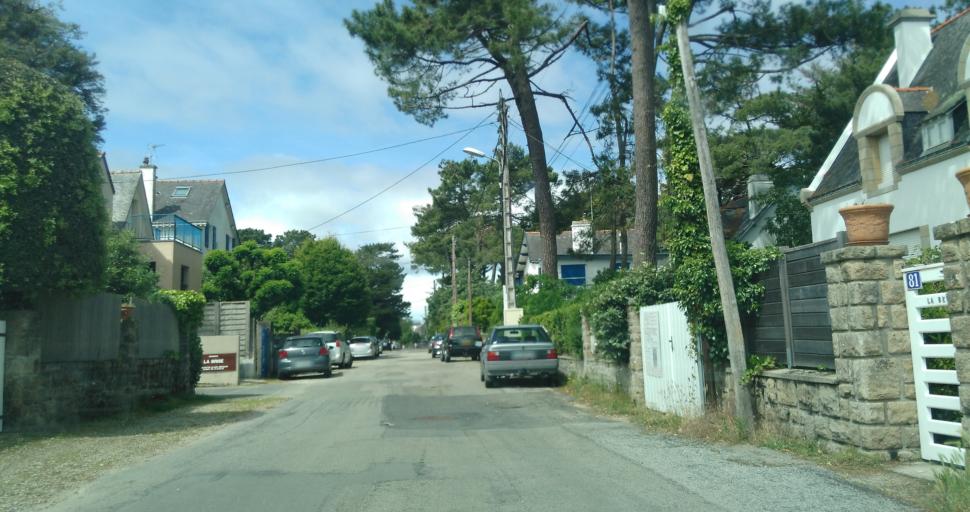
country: FR
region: Brittany
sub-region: Departement du Morbihan
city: Carnac
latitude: 47.5735
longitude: -3.0640
